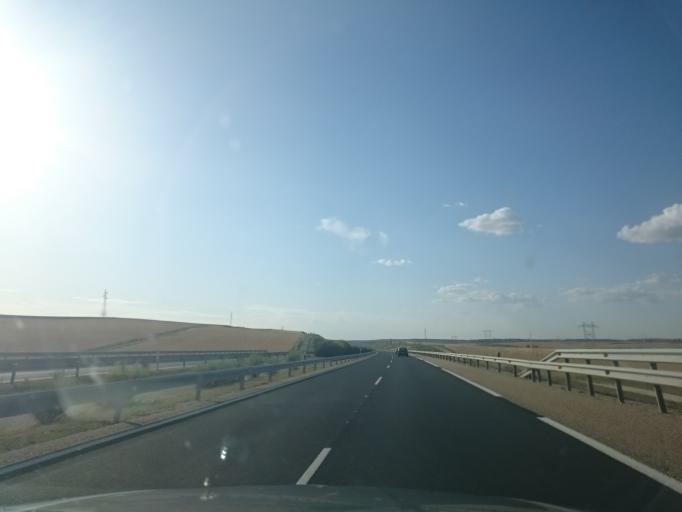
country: ES
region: Castille and Leon
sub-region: Provincia de Burgos
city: Villalbilla de Burgos
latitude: 42.3225
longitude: -3.7668
